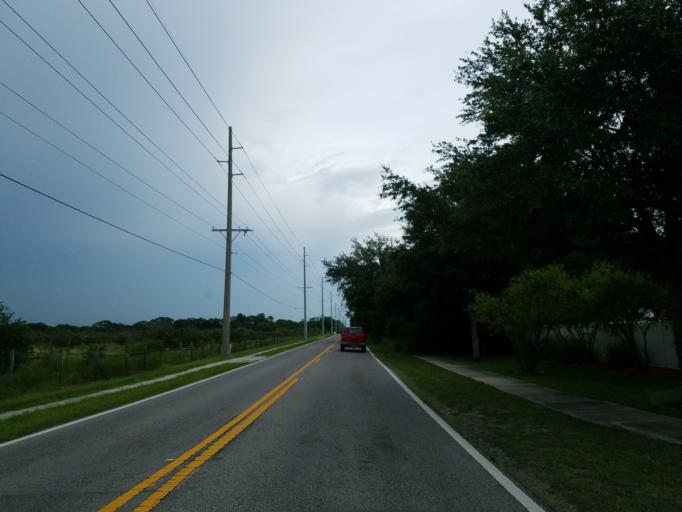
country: US
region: Florida
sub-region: Hillsborough County
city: Riverview
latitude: 27.8352
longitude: -82.3396
